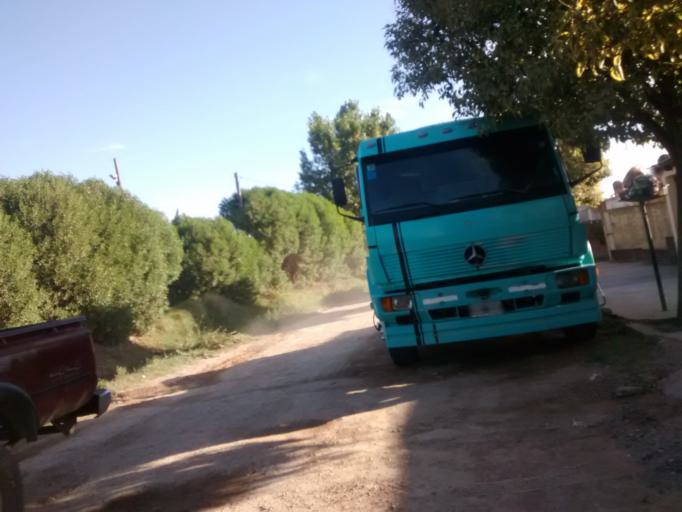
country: AR
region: Buenos Aires
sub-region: Partido de Loberia
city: Loberia
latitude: -38.1703
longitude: -58.7839
